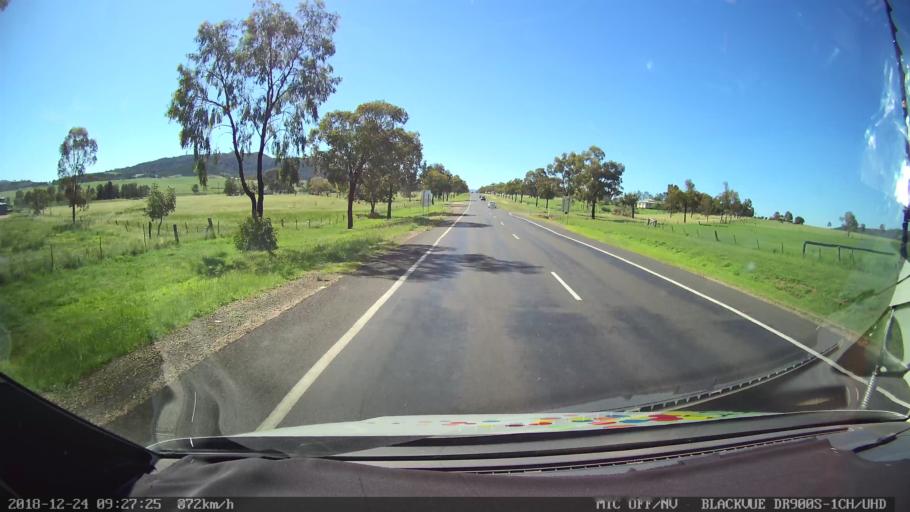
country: AU
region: New South Wales
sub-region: Liverpool Plains
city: Quirindi
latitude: -31.5279
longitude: 150.6810
